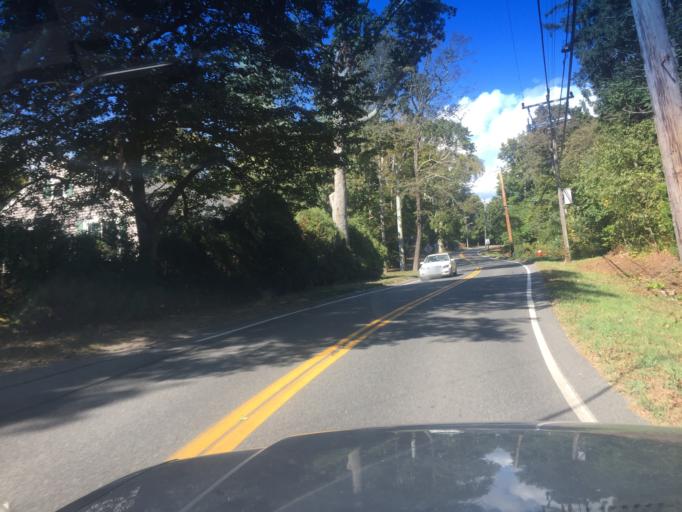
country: US
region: Massachusetts
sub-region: Barnstable County
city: Pocasset
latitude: 41.6794
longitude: -70.6133
